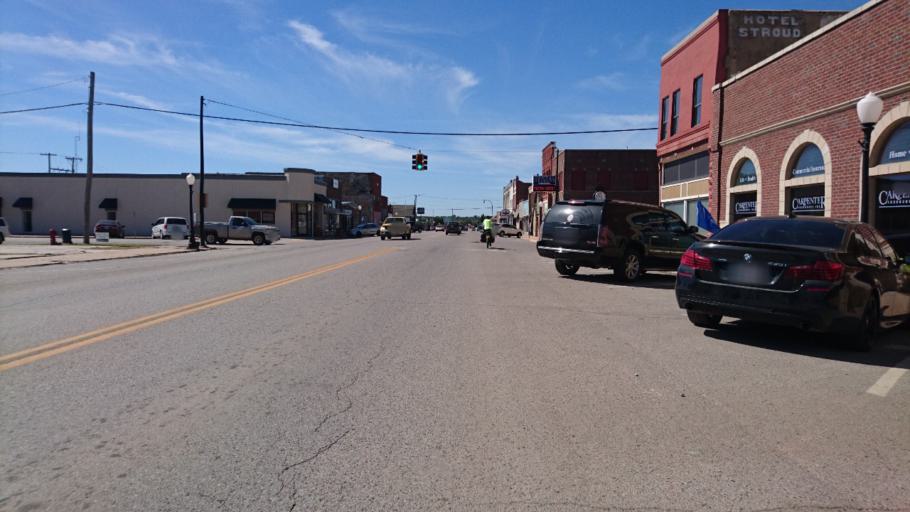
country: US
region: Oklahoma
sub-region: Lincoln County
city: Stroud
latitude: 35.7491
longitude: -96.6572
